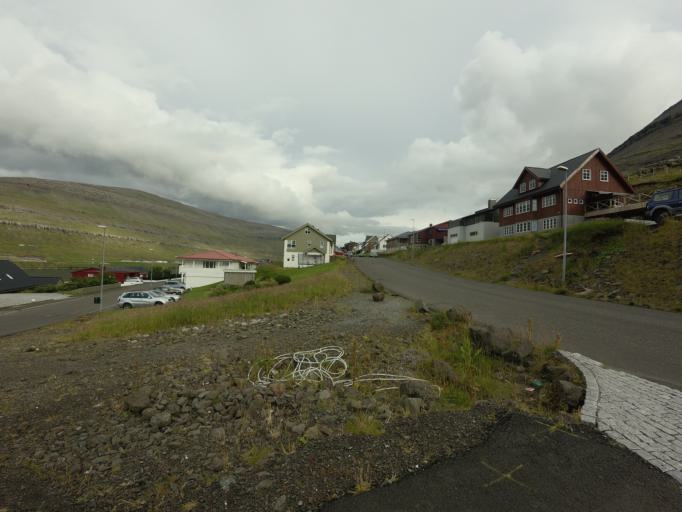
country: FO
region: Nordoyar
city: Klaksvik
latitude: 62.2212
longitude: -6.5824
